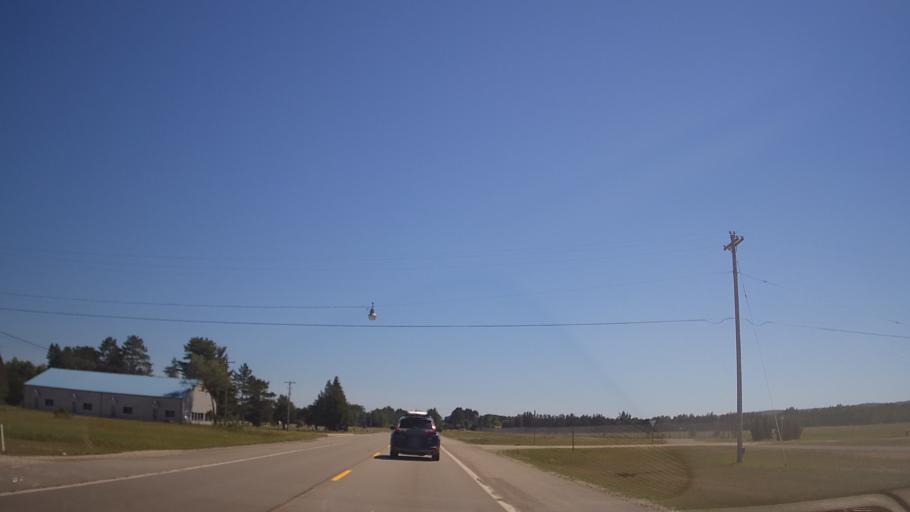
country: US
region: Michigan
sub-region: Cheboygan County
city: Indian River
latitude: 45.5645
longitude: -84.7840
